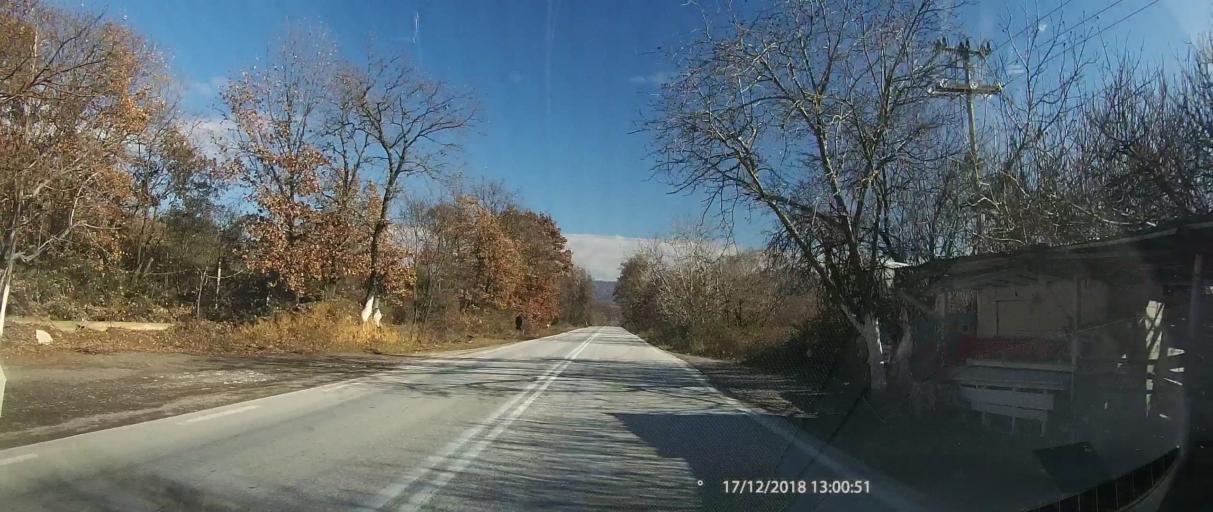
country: GR
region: Thessaly
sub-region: Trikala
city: Kastraki
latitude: 39.7317
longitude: 21.5722
